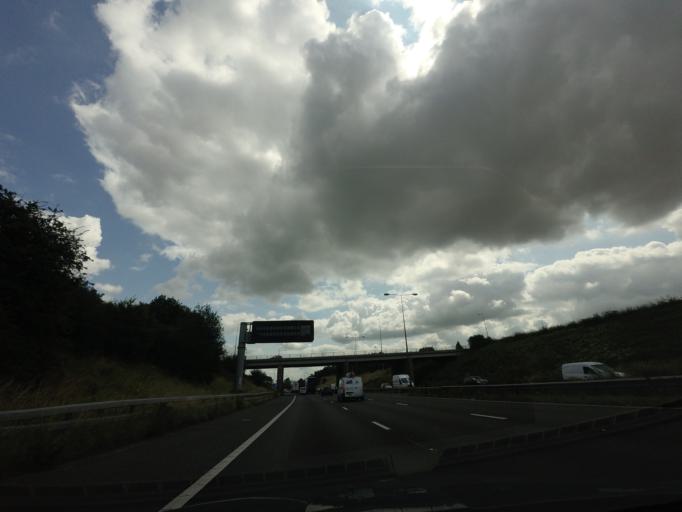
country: GB
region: England
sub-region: St. Helens
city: Billinge
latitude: 53.5138
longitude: -2.6887
